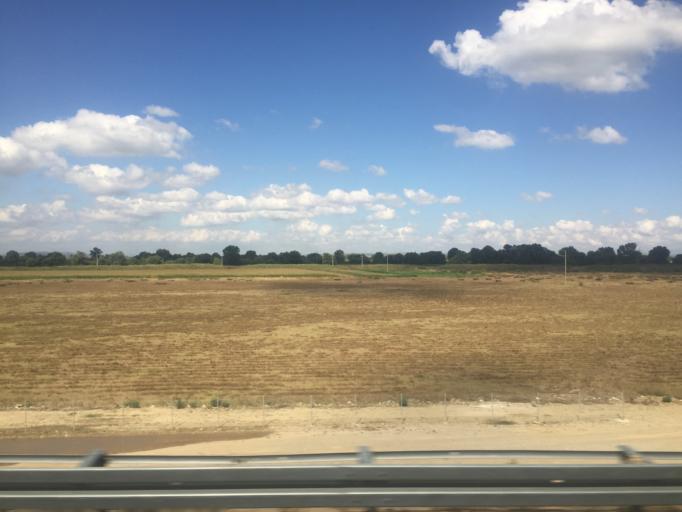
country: TR
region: Bursa
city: Tatkavakli
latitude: 40.1166
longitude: 28.2780
